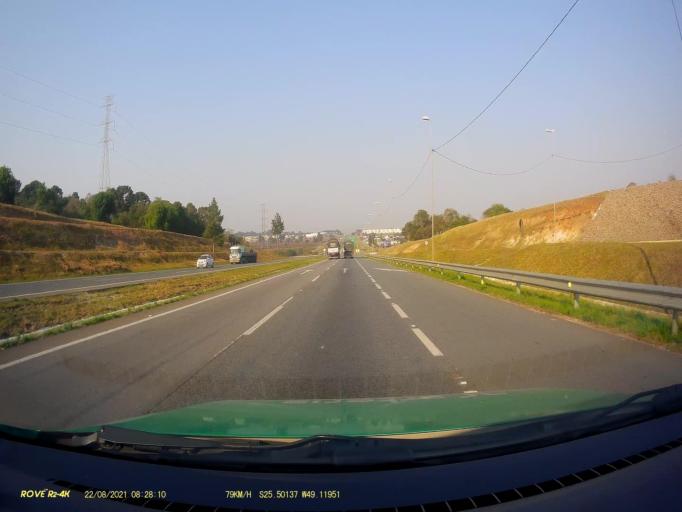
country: BR
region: Parana
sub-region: Piraquara
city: Piraquara
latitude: -25.5015
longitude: -49.1196
